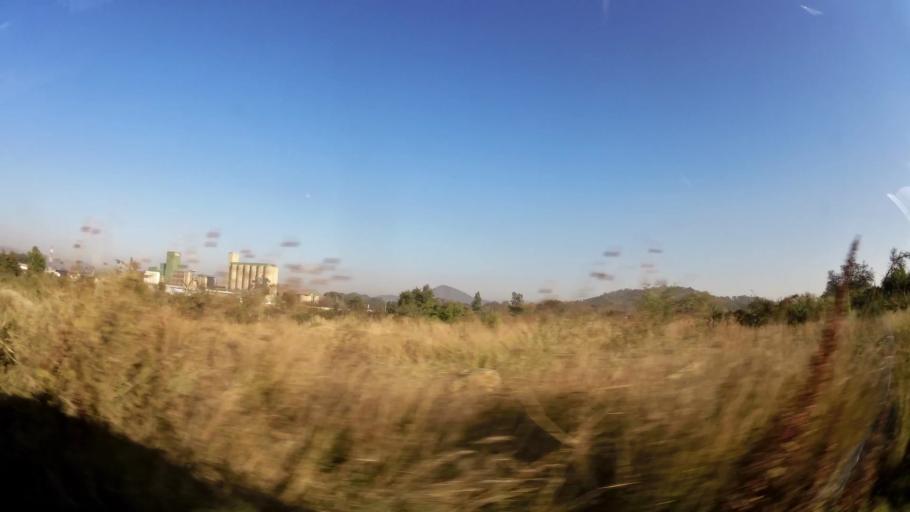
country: ZA
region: Gauteng
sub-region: City of Tshwane Metropolitan Municipality
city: Pretoria
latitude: -25.6314
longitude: 28.2049
